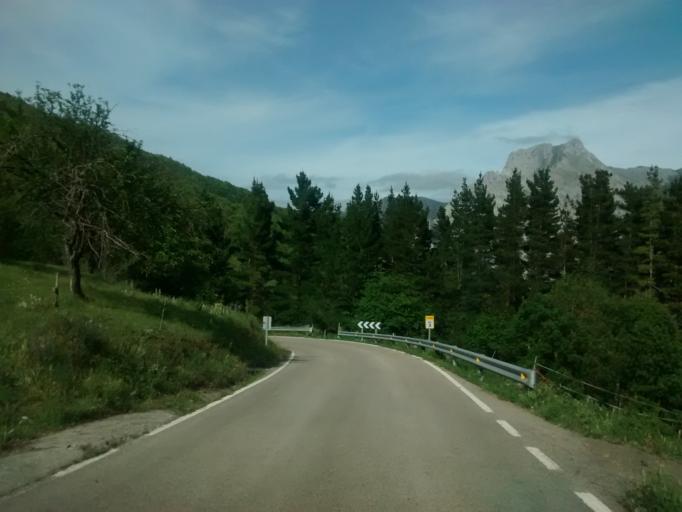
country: ES
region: Cantabria
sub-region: Provincia de Cantabria
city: Potes
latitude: 43.1913
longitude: -4.6304
